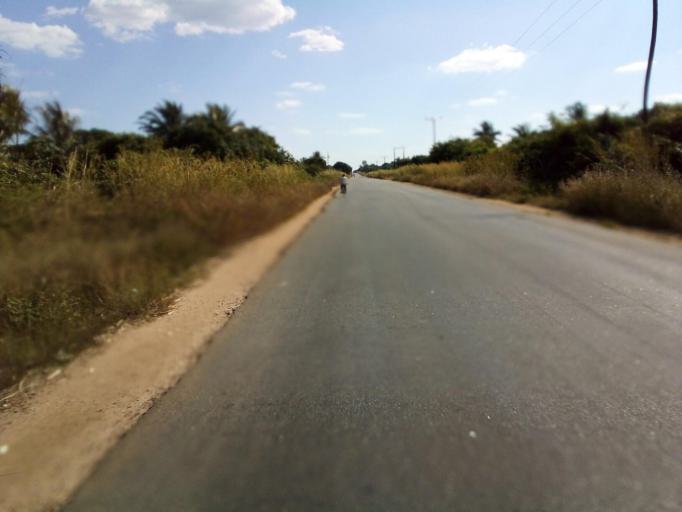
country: MZ
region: Zambezia
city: Quelimane
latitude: -17.5775
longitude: 36.6705
